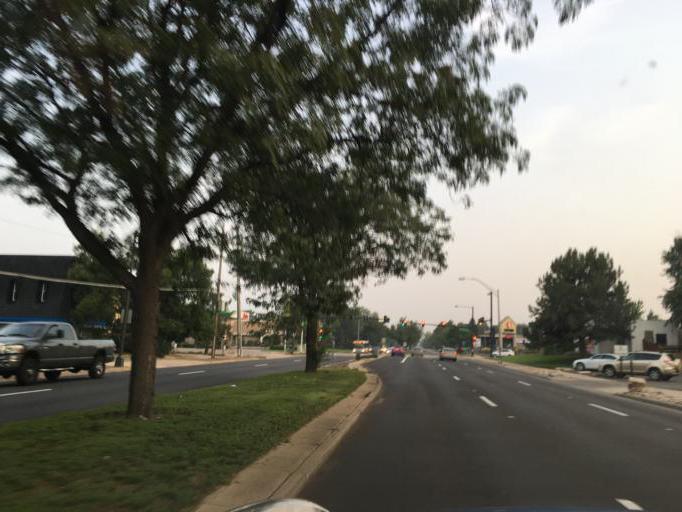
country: US
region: Colorado
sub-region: Arapahoe County
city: Glendale
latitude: 39.6688
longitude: -104.9130
